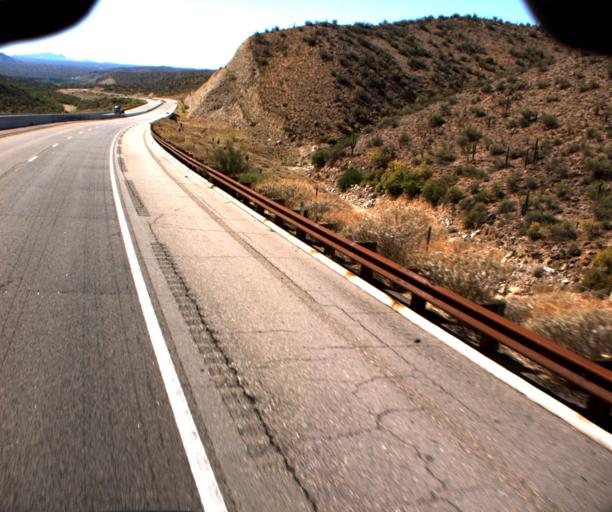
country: US
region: Arizona
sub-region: Yavapai County
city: Bagdad
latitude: 34.4051
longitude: -113.2227
